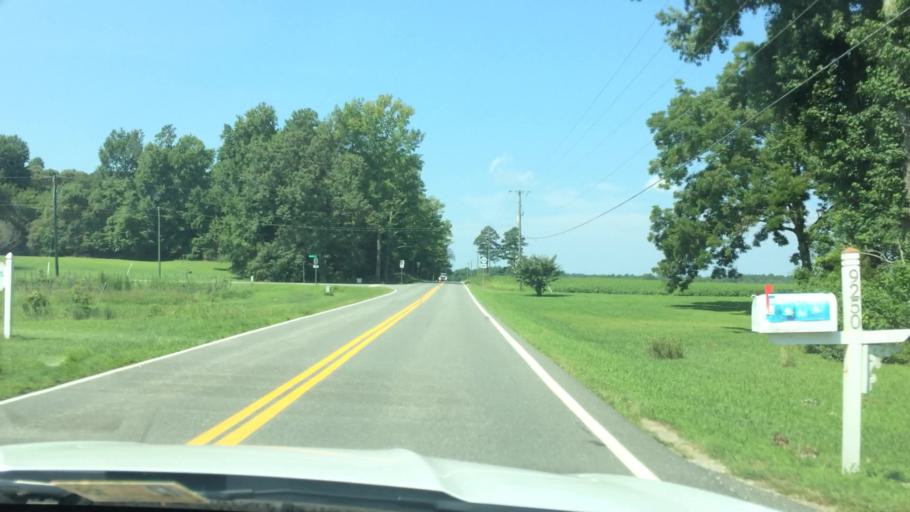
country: US
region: Virginia
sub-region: New Kent County
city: New Kent
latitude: 37.5258
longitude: -77.0378
